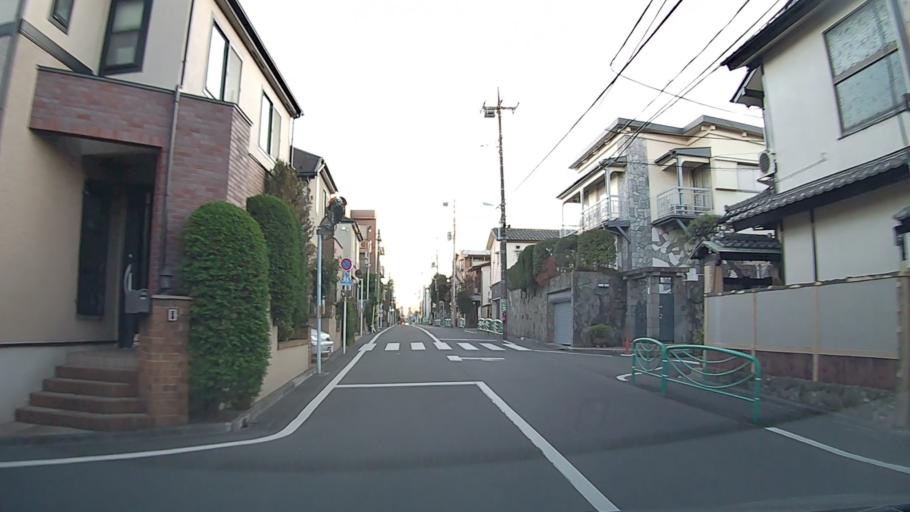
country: JP
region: Tokyo
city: Musashino
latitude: 35.7169
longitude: 139.6110
